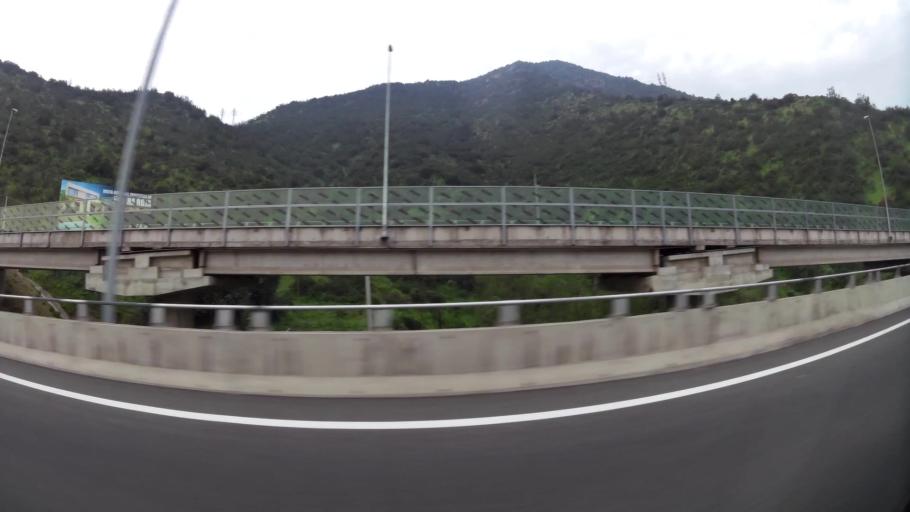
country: CL
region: Santiago Metropolitan
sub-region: Provincia de Santiago
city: Santiago
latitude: -33.3706
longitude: -70.6101
